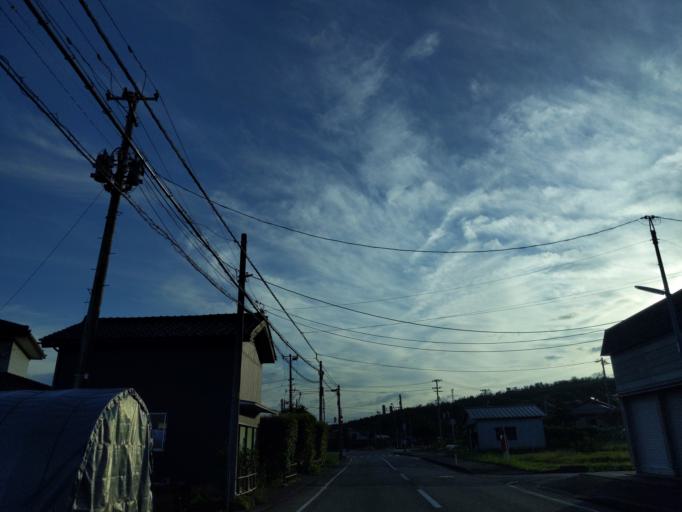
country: JP
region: Niigata
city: Kashiwazaki
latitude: 37.4319
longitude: 138.6204
